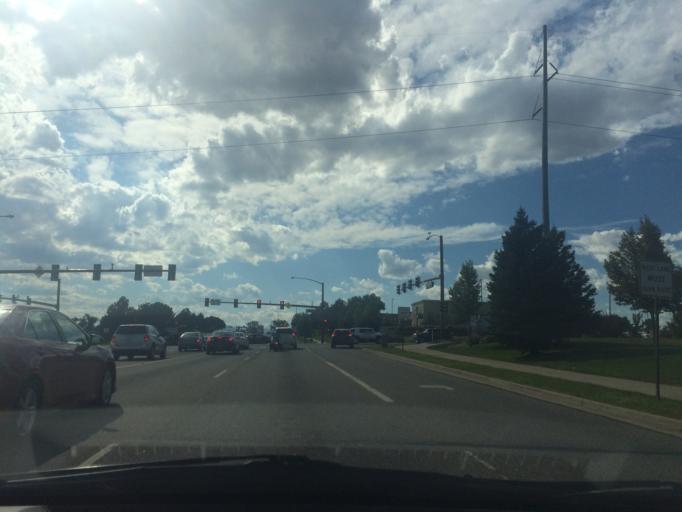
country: US
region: Colorado
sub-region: Adams County
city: Thornton
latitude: 39.8708
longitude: -104.9769
